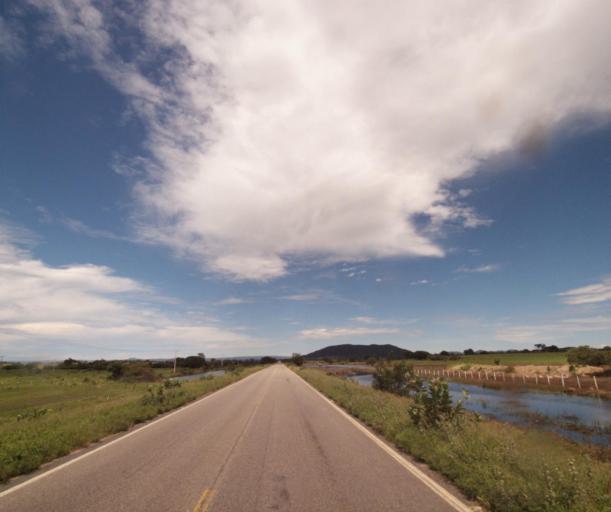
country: BR
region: Bahia
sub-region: Guanambi
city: Guanambi
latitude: -14.2289
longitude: -42.9217
